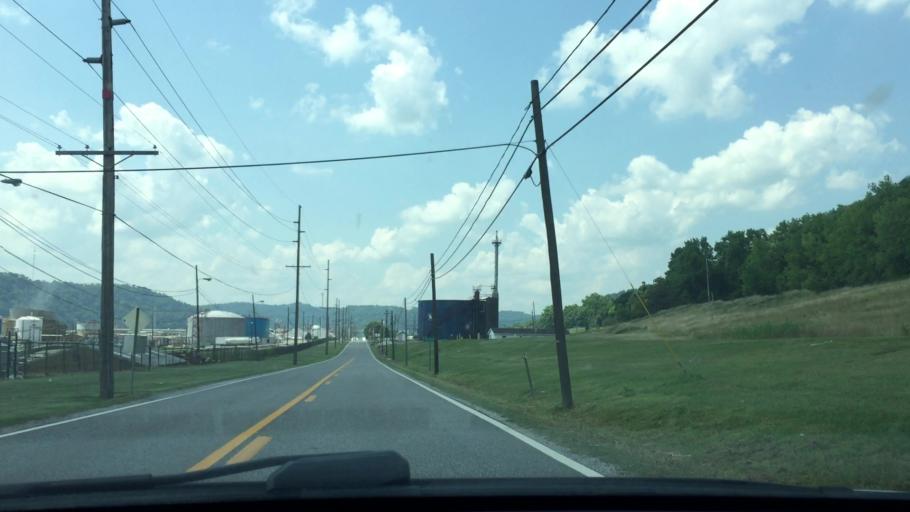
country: US
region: West Virginia
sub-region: Wetzel County
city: New Martinsville
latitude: 39.7437
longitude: -80.8447
